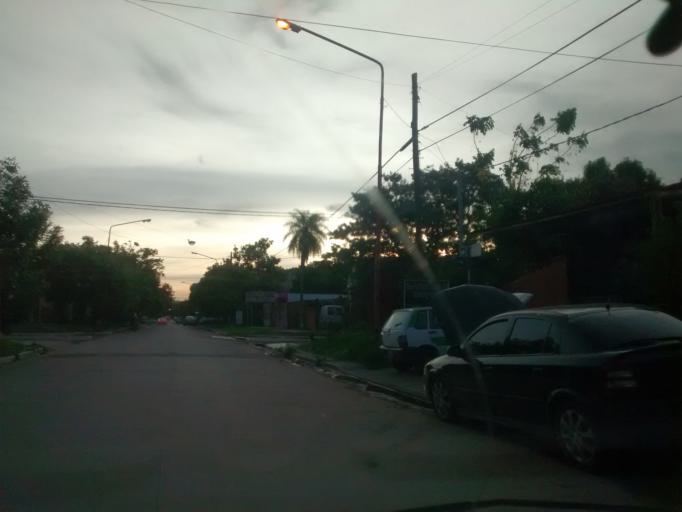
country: AR
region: Chaco
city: Resistencia
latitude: -27.4358
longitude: -58.9926
